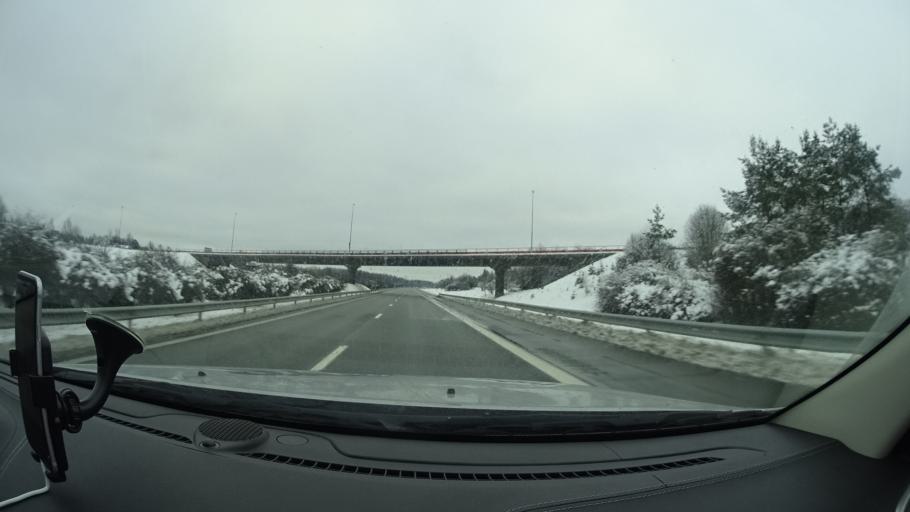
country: SE
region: Joenkoeping
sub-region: Vaggeryds Kommun
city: Skillingaryd
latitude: 57.4165
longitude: 14.1011
